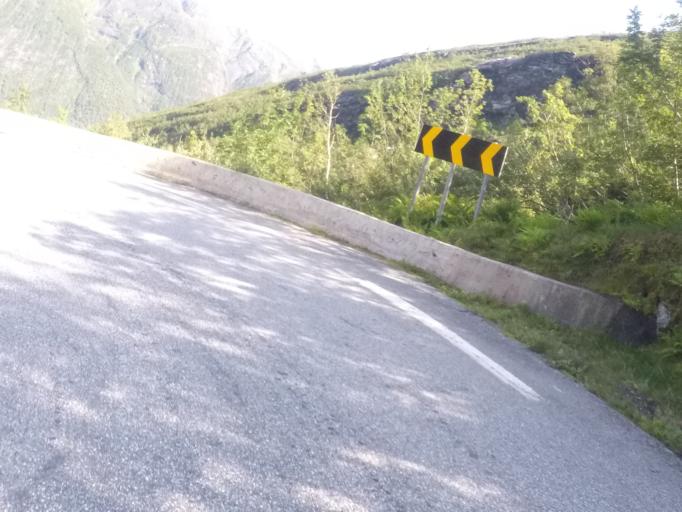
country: NO
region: Sogn og Fjordane
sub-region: Balestrand
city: Balestrand
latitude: 61.3530
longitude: 6.5231
